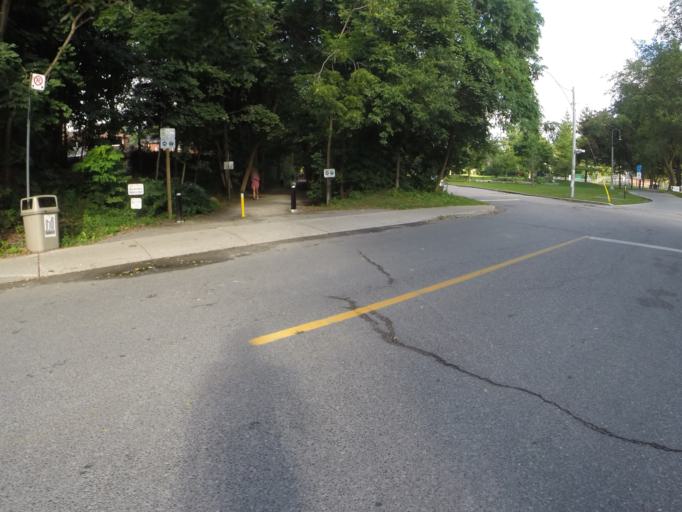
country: CA
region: Ontario
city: Toronto
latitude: 43.6964
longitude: -79.3995
